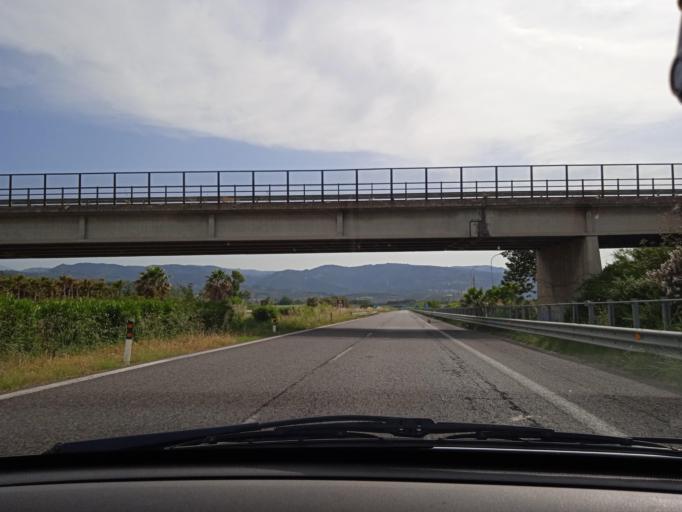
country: IT
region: Sicily
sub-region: Messina
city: Vigliatore 2
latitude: 38.1255
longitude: 15.1240
